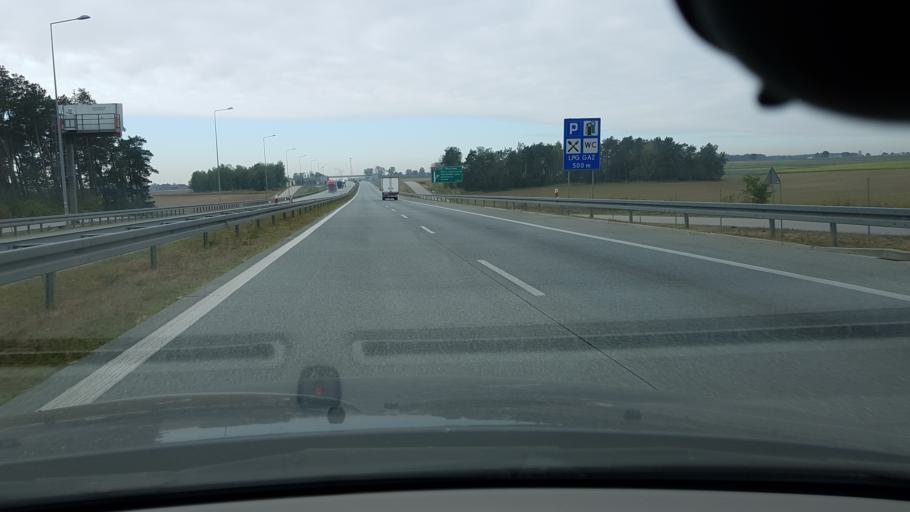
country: PL
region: Lodz Voivodeship
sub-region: Powiat tomaszowski
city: Czerniewice
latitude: 51.6843
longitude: 20.1986
